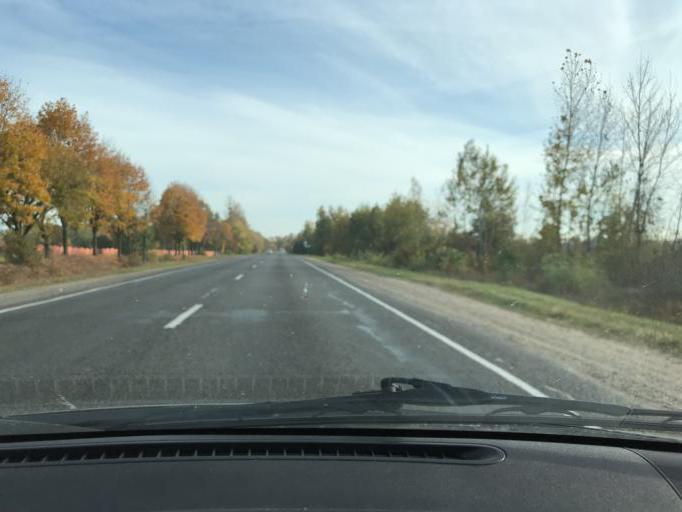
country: BY
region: Brest
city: Asnyezhytsy
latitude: 52.2018
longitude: 26.0612
